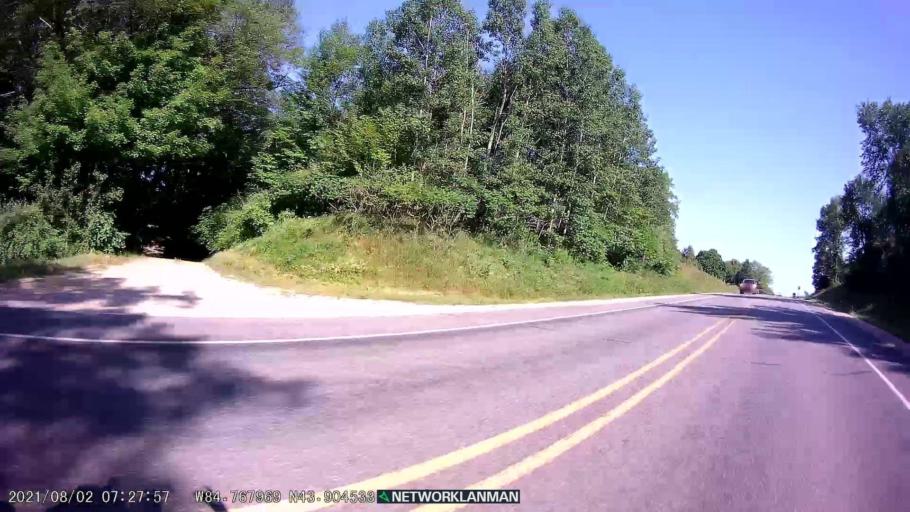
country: US
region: Michigan
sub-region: Clare County
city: Clare
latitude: 43.9042
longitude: -84.7679
